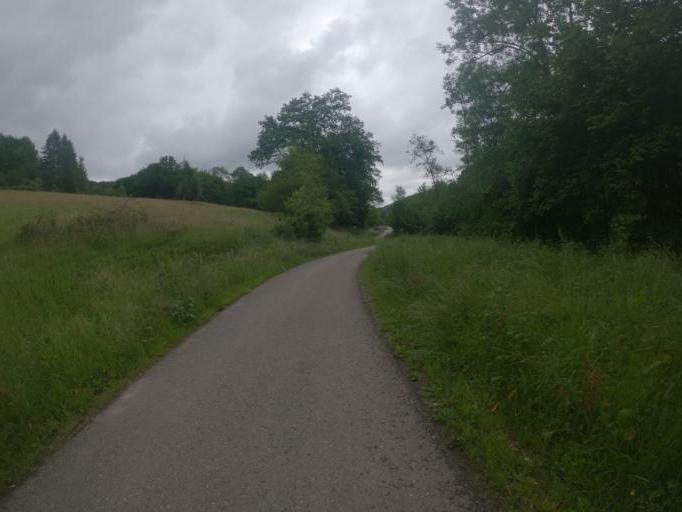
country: DE
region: Baden-Wuerttemberg
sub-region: Regierungsbezirk Stuttgart
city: Ebersbach an der Fils
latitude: 48.7485
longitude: 9.5393
